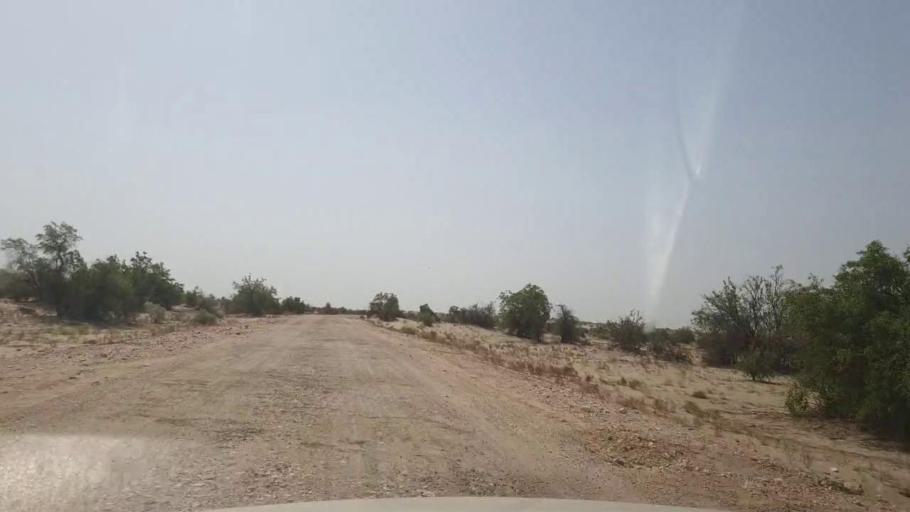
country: PK
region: Sindh
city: Rohri
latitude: 27.4416
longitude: 69.2408
